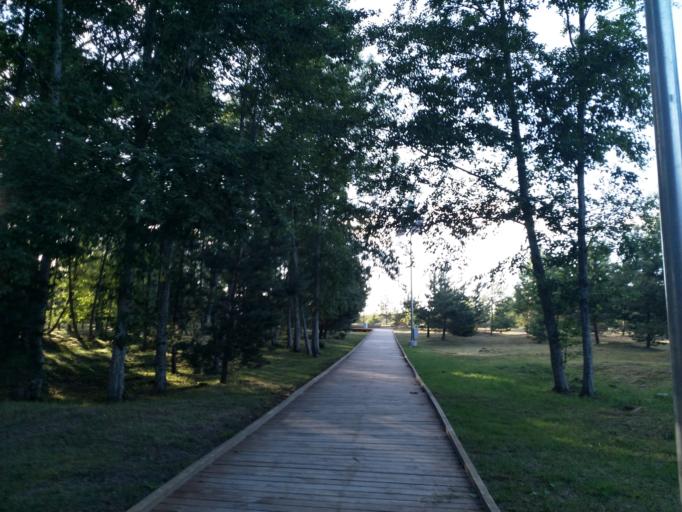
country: LV
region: Rojas
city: Roja
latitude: 57.5098
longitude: 22.8008
